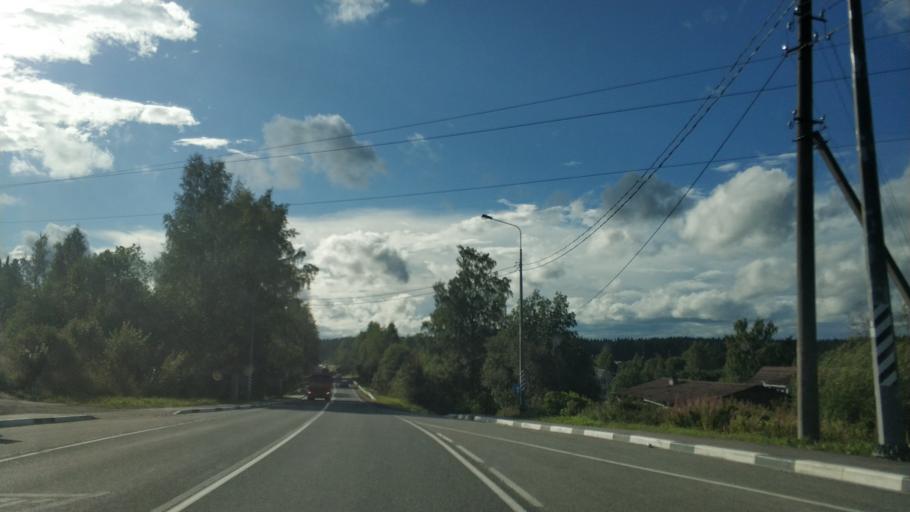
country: RU
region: Republic of Karelia
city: Lakhdenpokh'ya
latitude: 61.5229
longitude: 30.1769
